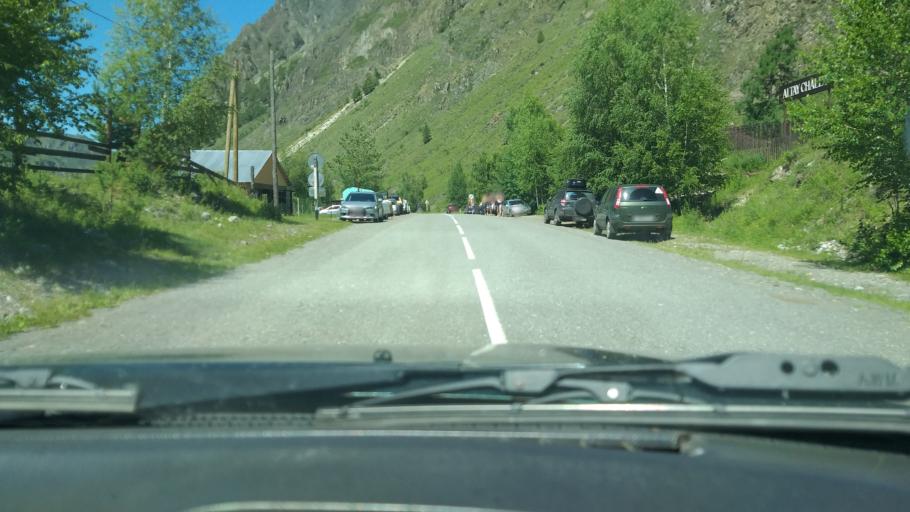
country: RU
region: Altay
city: Chemal
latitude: 51.2608
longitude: 86.0696
